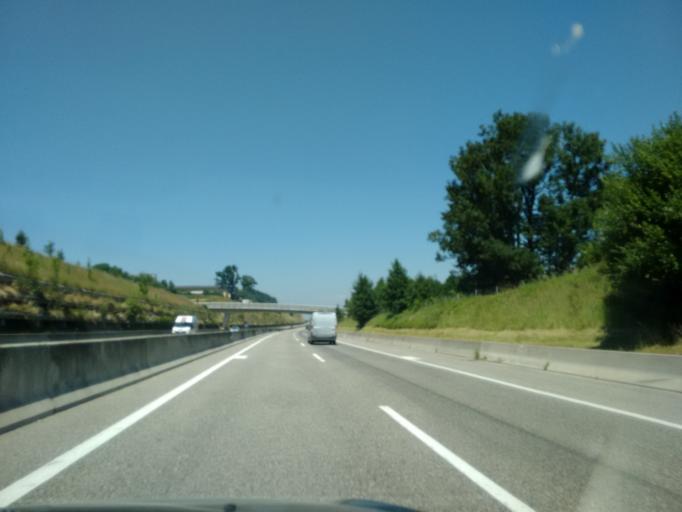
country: AT
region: Upper Austria
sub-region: Wels-Land
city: Steinhaus
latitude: 48.0866
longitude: 14.0198
